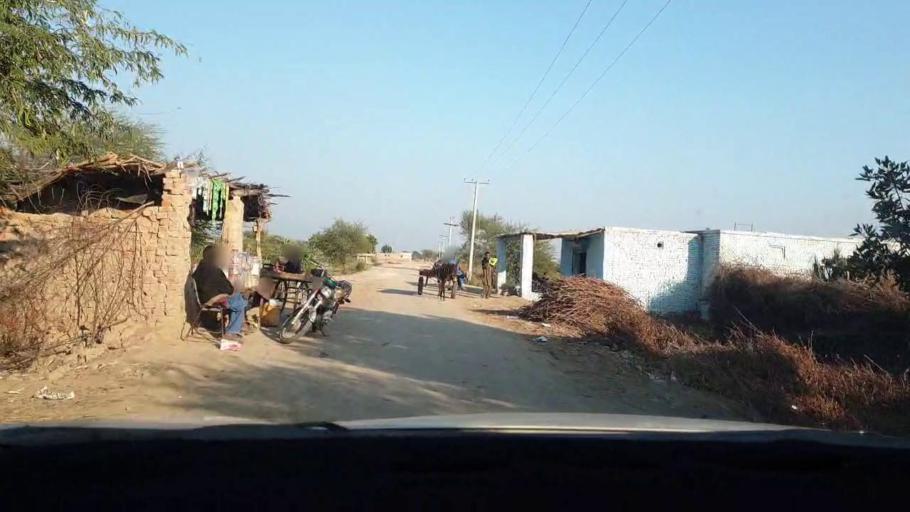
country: PK
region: Sindh
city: Tando Adam
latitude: 25.7460
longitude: 68.7351
